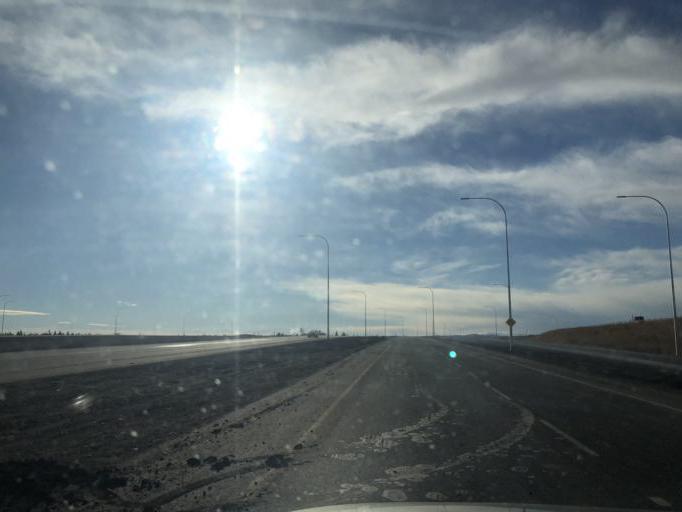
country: CA
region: Alberta
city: Calgary
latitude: 50.9559
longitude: -114.1429
